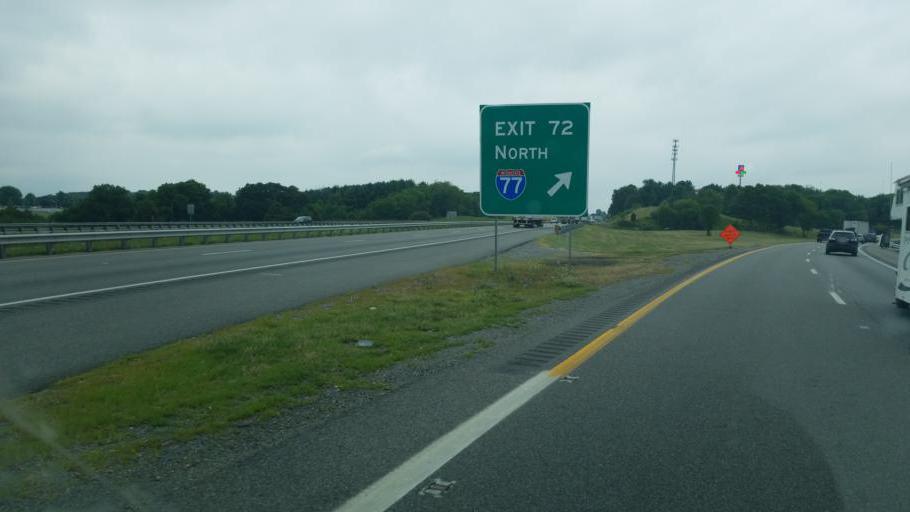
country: US
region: Virginia
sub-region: Wythe County
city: Wytheville
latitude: 36.9603
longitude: -81.0624
